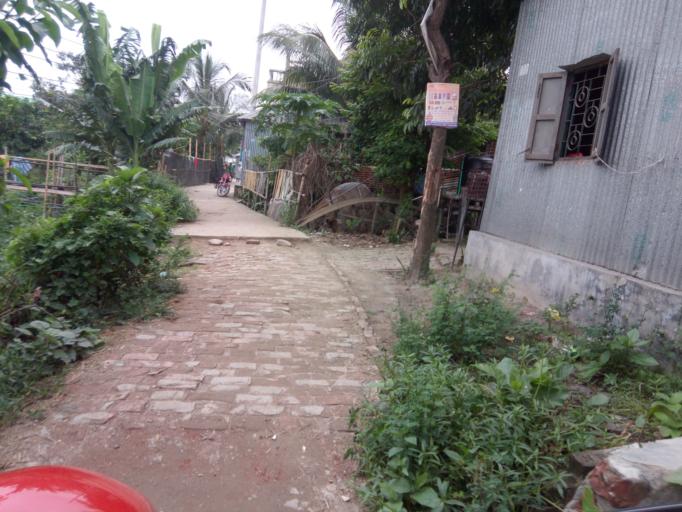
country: BD
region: Dhaka
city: Paltan
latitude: 23.7478
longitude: 90.4618
